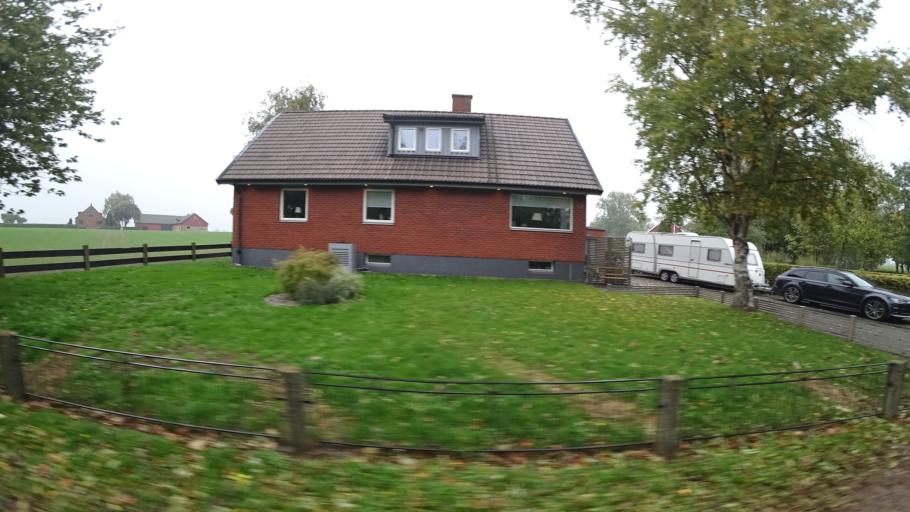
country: SE
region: Skane
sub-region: Kavlinge Kommun
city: Kaevlinge
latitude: 55.8043
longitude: 13.1526
